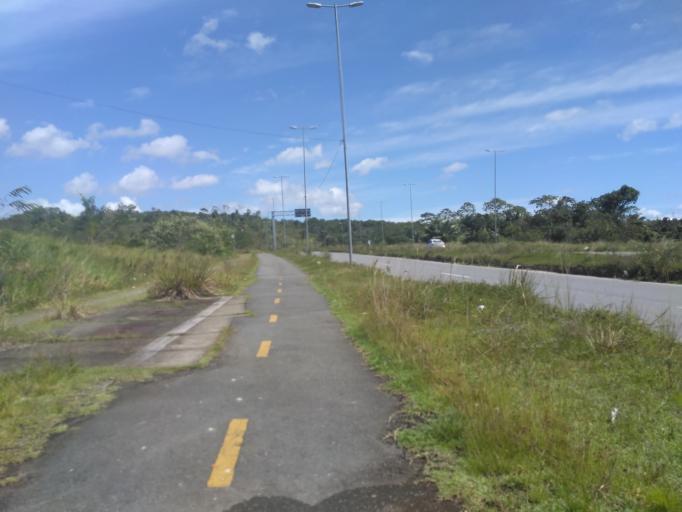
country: BR
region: Pernambuco
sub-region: Sao Lourenco Da Mata
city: Sao Lourenco da Mata
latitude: -8.0444
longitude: -35.0003
